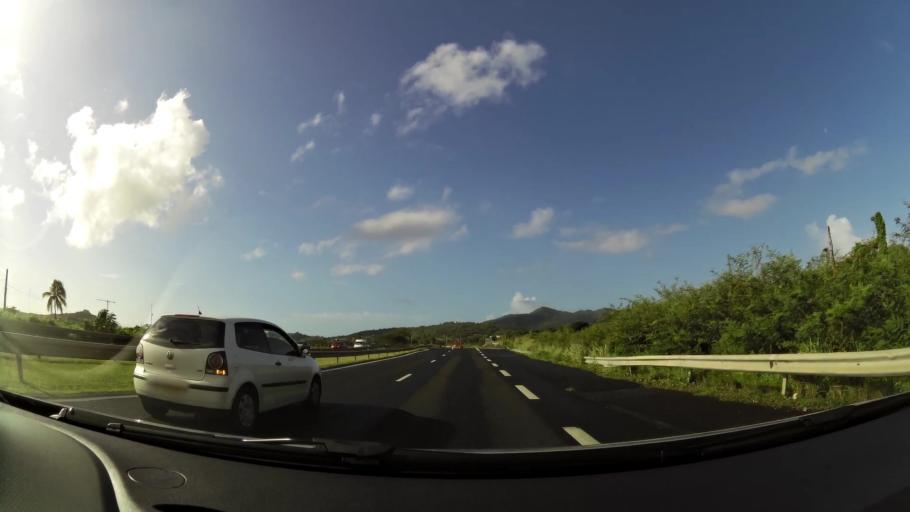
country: MQ
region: Martinique
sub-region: Martinique
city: Ducos
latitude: 14.5354
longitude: -60.9812
